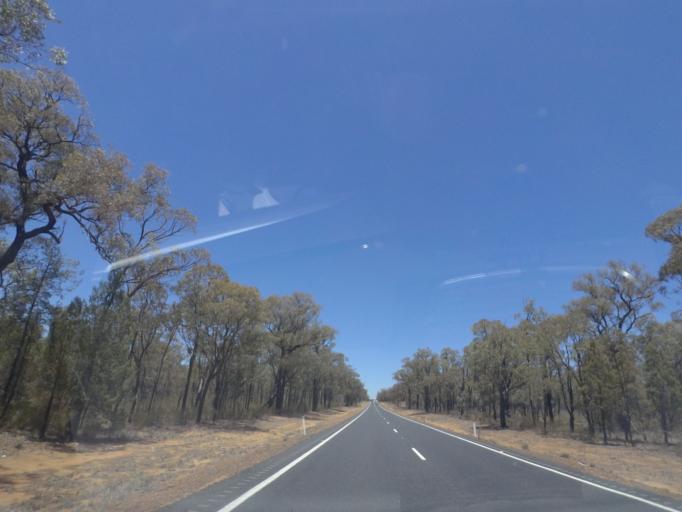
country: AU
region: New South Wales
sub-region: Narrabri
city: Narrabri
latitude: -30.7386
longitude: 149.5167
